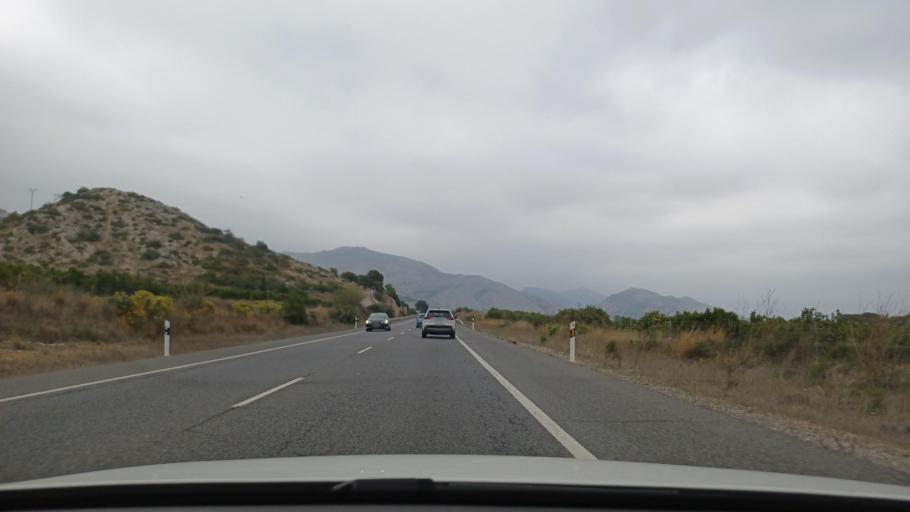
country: ES
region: Valencia
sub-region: Provincia de Castello
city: Borriol
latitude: 40.0228
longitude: -0.0381
